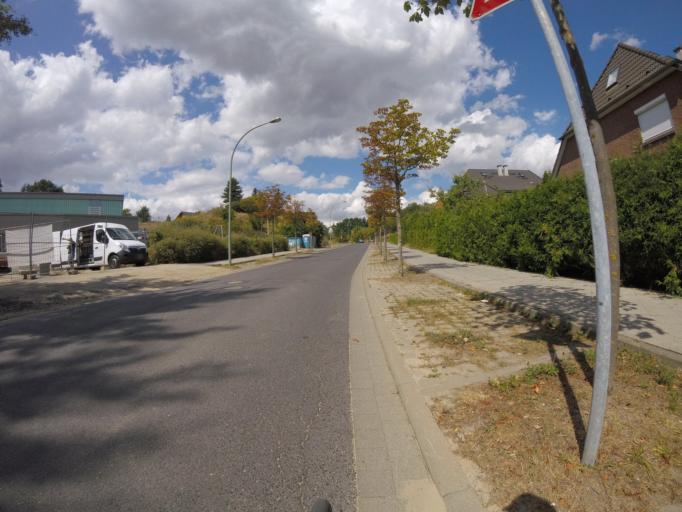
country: DE
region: Brandenburg
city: Werder
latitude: 52.4065
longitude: 12.9946
